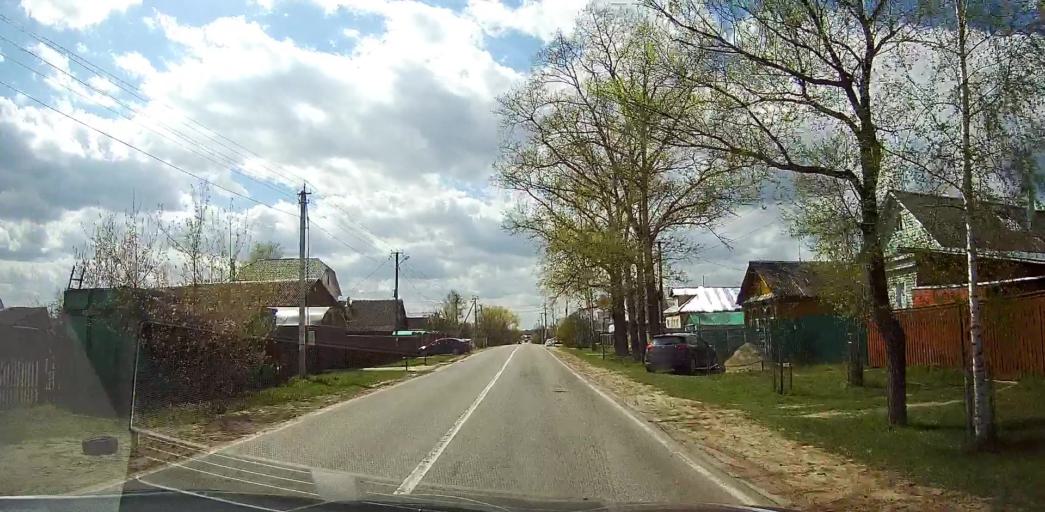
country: RU
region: Moskovskaya
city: Davydovo
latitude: 55.5553
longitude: 38.8161
